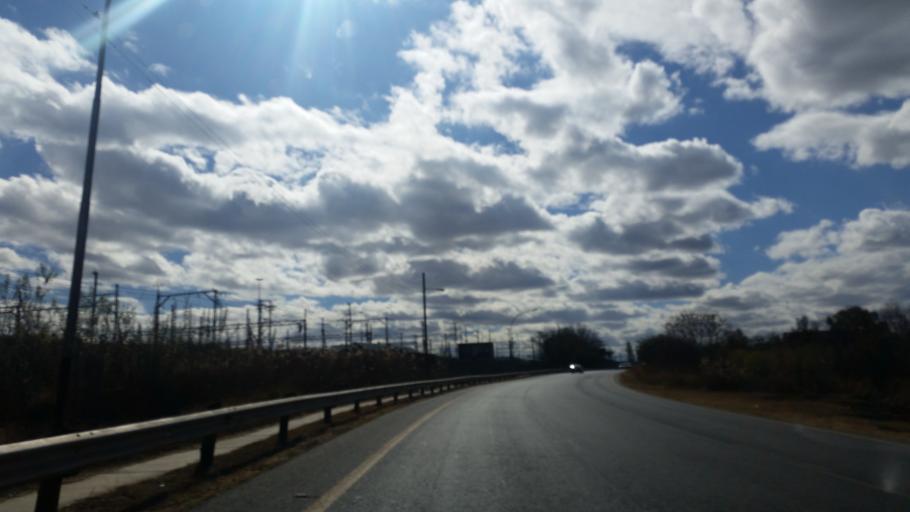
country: ZA
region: KwaZulu-Natal
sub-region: uThukela District Municipality
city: Ladysmith
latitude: -28.5447
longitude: 29.7941
